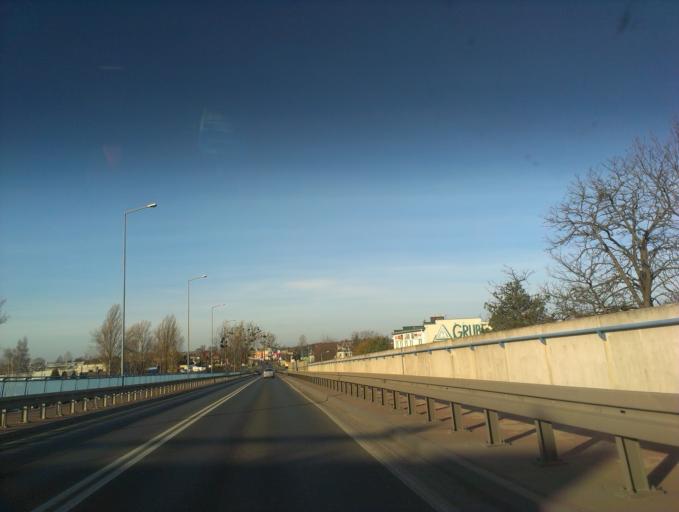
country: PL
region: Greater Poland Voivodeship
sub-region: Powiat poznanski
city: Suchy Las
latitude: 52.4651
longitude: 16.8883
